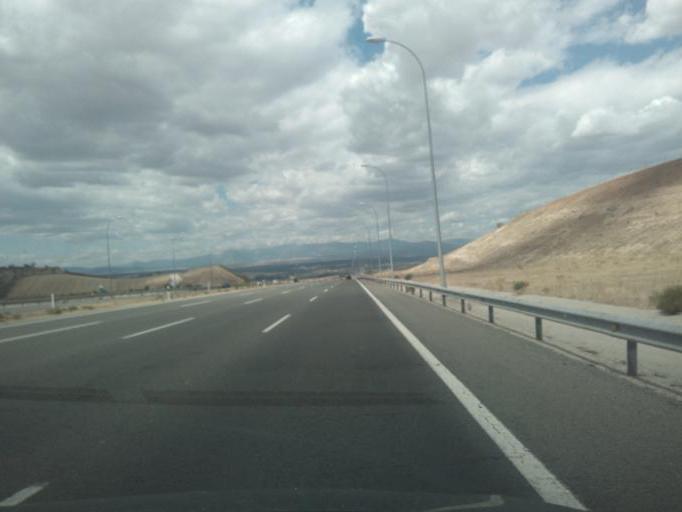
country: ES
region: Madrid
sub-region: Provincia de Madrid
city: Paracuellos de Jarama
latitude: 40.5316
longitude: -3.5201
